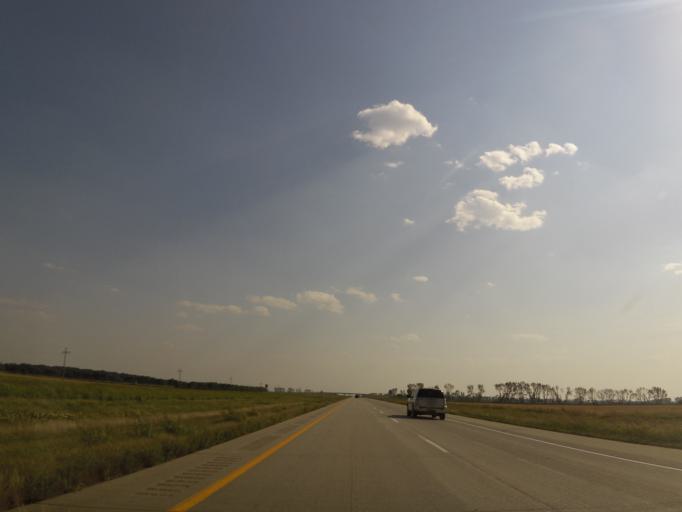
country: US
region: North Dakota
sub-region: Walsh County
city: Grafton
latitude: 48.2489
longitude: -97.1895
